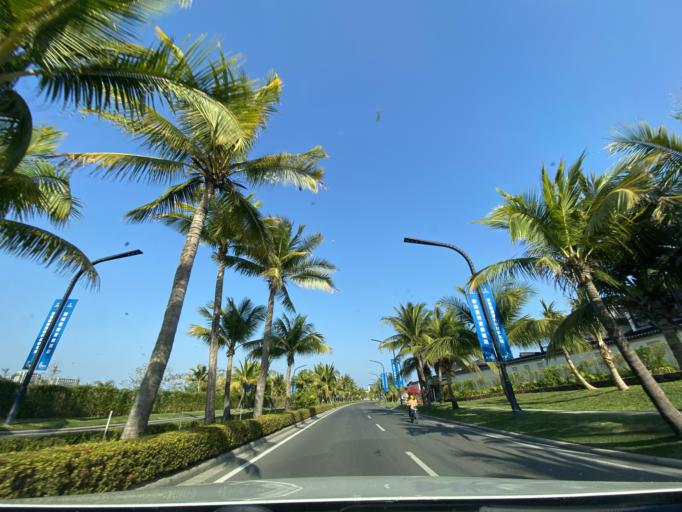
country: CN
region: Hainan
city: Xincun
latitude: 18.4233
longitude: 109.9524
